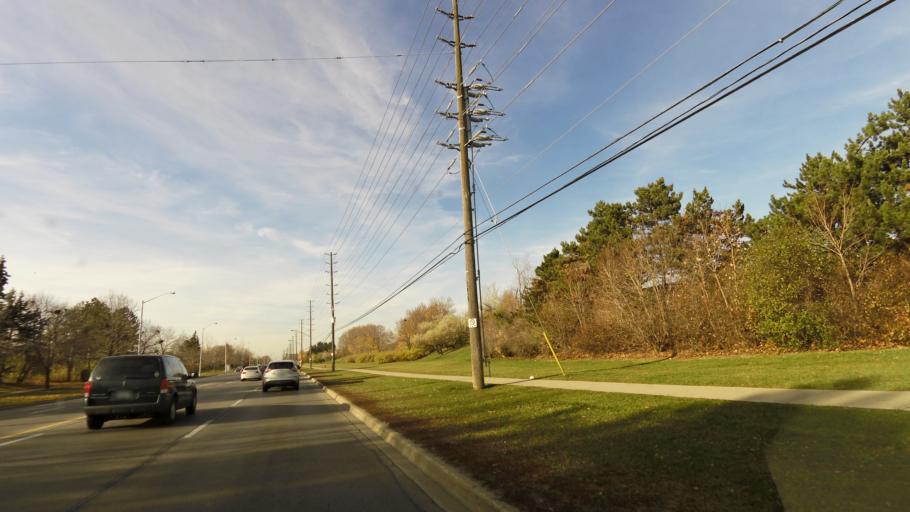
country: CA
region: Ontario
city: Brampton
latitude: 43.7459
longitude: -79.7224
